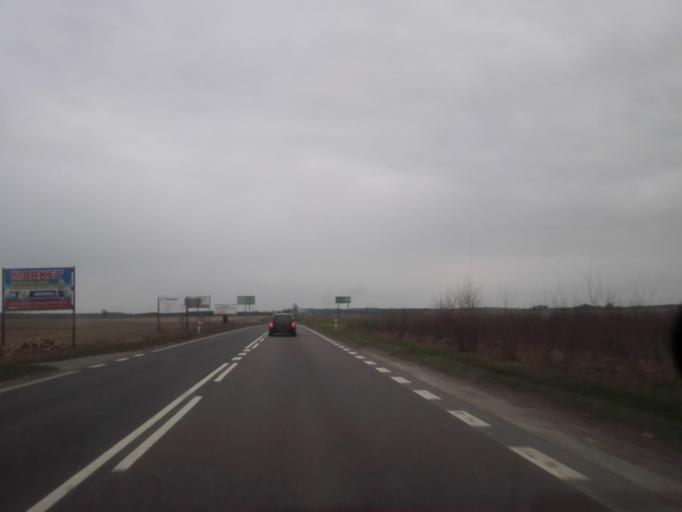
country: PL
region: Podlasie
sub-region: Powiat grajewski
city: Grajewo
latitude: 53.6384
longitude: 22.4355
